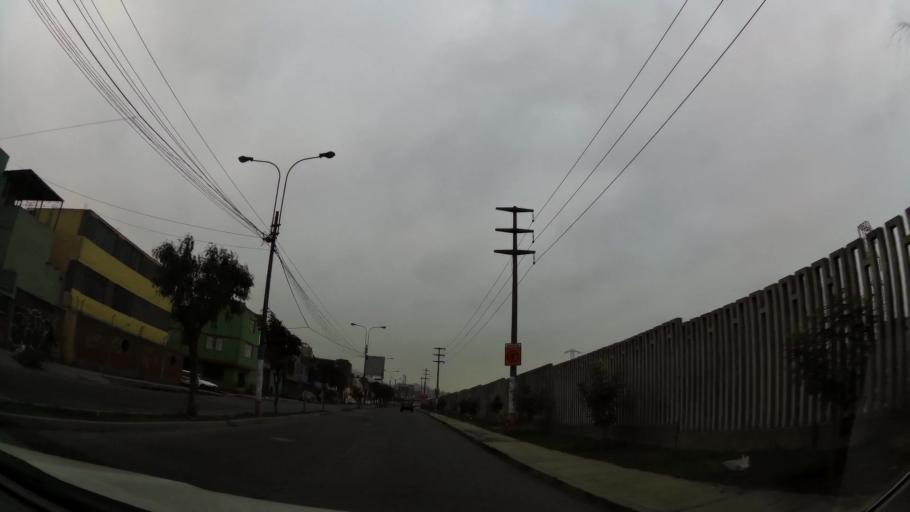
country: PE
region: Lima
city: Lima
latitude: -12.0286
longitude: -77.0031
